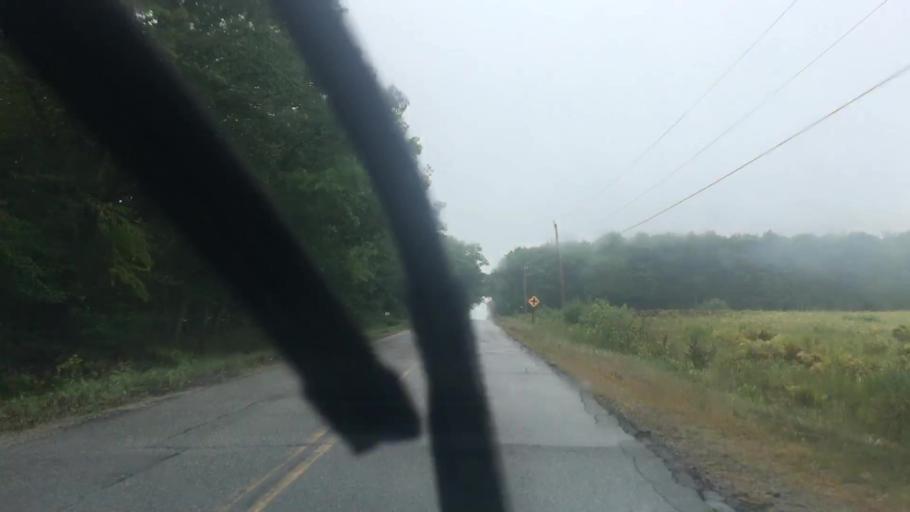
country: US
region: Maine
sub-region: Waldo County
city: Stockton Springs
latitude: 44.5412
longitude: -68.9128
